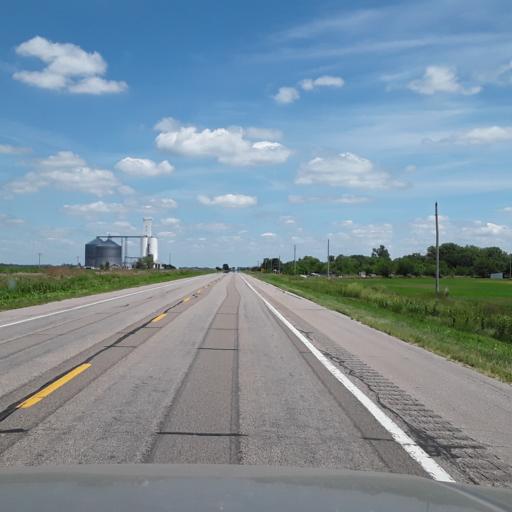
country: US
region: Nebraska
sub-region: Nance County
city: Genoa
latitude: 41.3241
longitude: -97.6444
